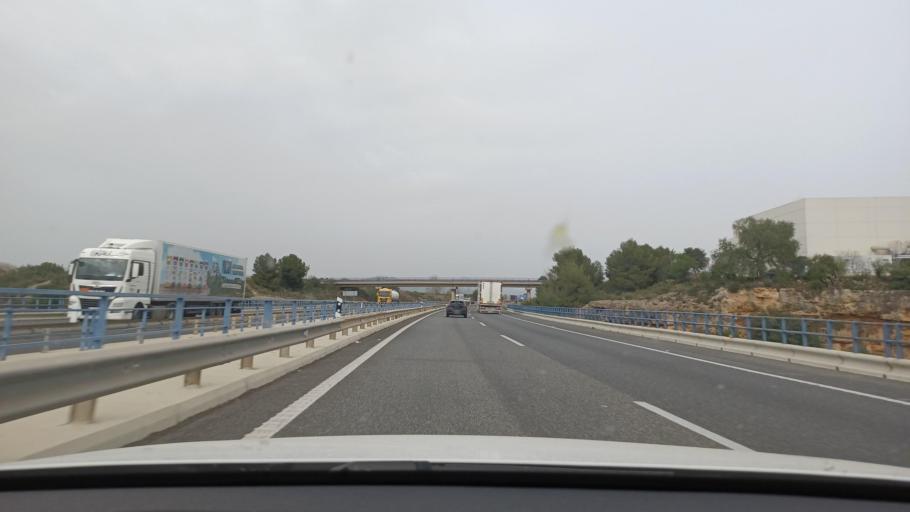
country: ES
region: Valencia
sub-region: Provincia de Castello
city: Vila-real
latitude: 39.9716
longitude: -0.1146
